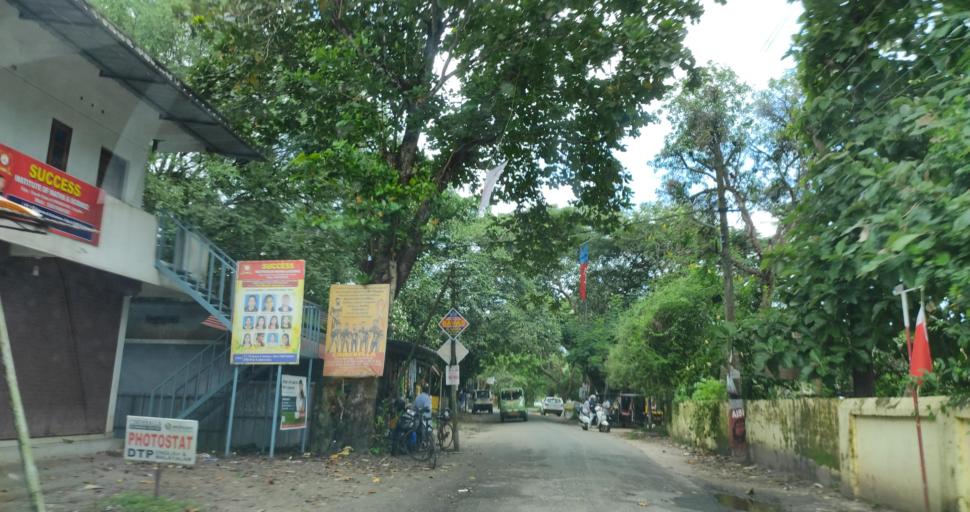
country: IN
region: Kerala
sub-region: Alappuzha
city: Vayalar
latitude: 9.7185
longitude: 76.3375
